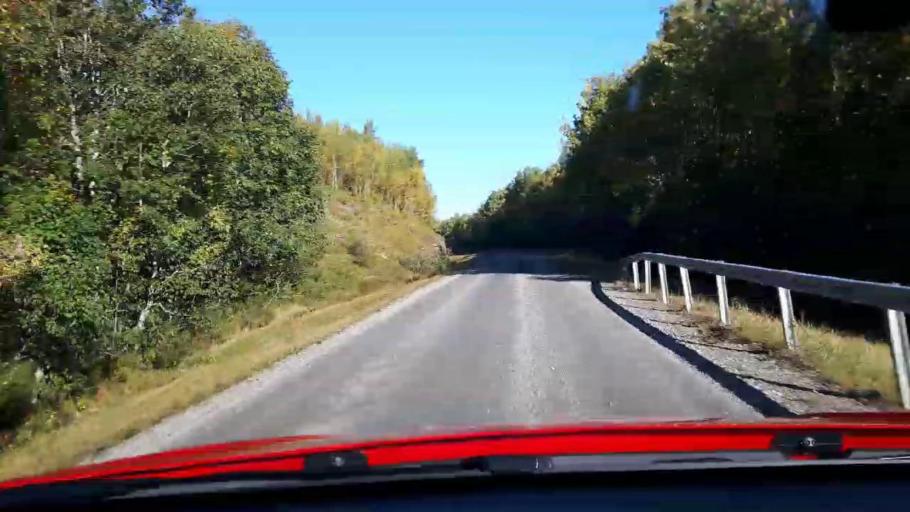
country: NO
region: Nord-Trondelag
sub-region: Lierne
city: Sandvika
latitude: 64.5711
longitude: 13.9029
